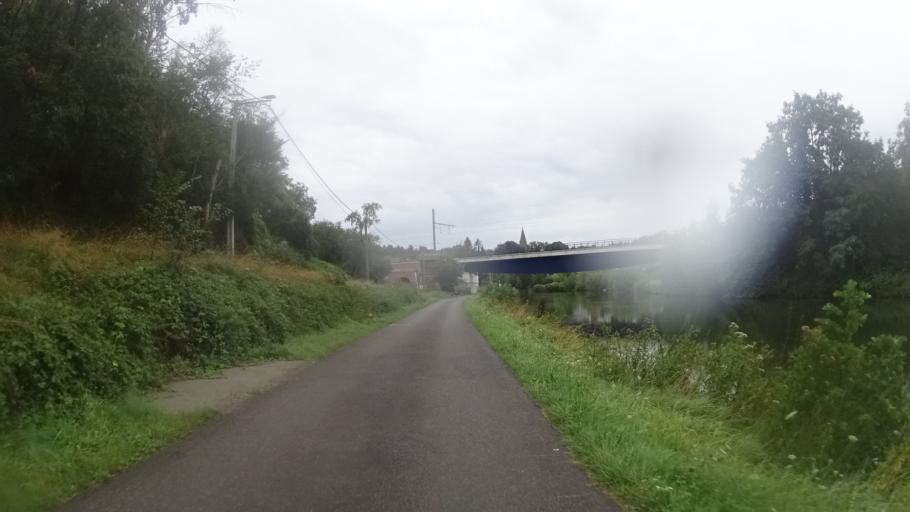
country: BE
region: Wallonia
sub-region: Province du Hainaut
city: Thuin
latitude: 50.3448
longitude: 4.2811
